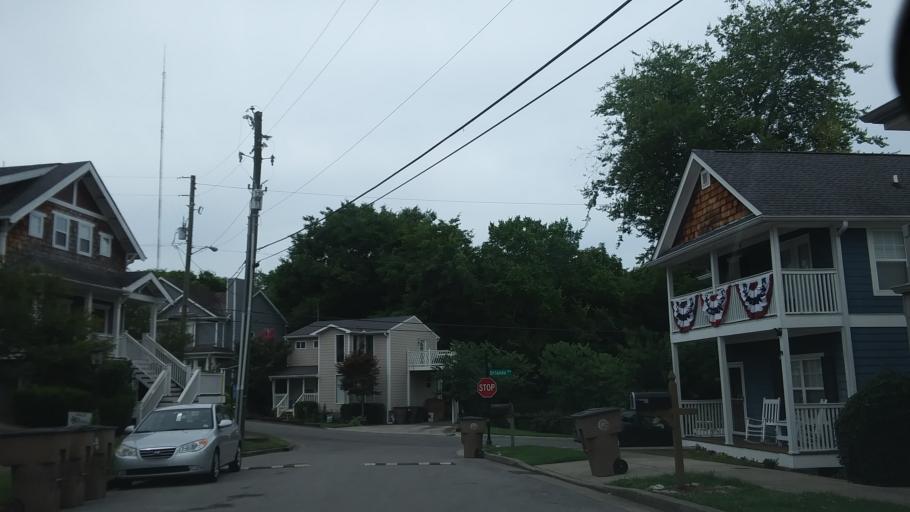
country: US
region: Tennessee
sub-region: Davidson County
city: Belle Meade
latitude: 36.1477
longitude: -86.8561
